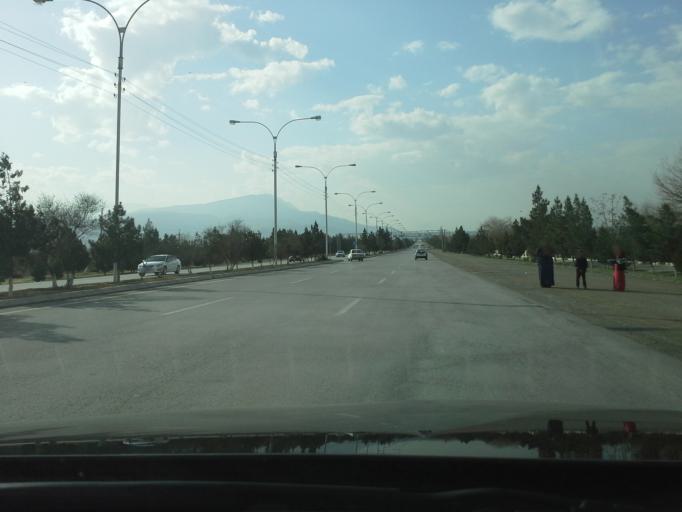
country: TM
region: Ahal
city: Abadan
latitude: 37.9719
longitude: 58.2605
